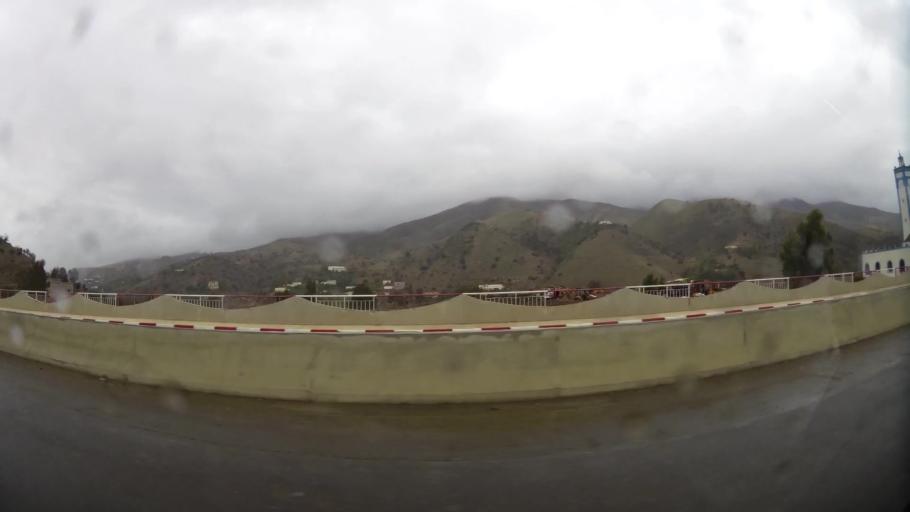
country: MA
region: Taza-Al Hoceima-Taounate
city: Imzourene
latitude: 35.0186
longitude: -3.8204
